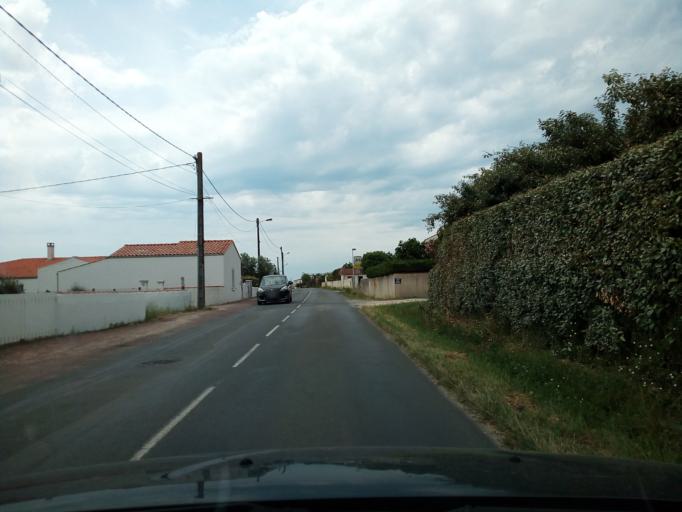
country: FR
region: Poitou-Charentes
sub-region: Departement de la Charente-Maritime
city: Dolus-d'Oleron
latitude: 45.9216
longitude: -1.3277
